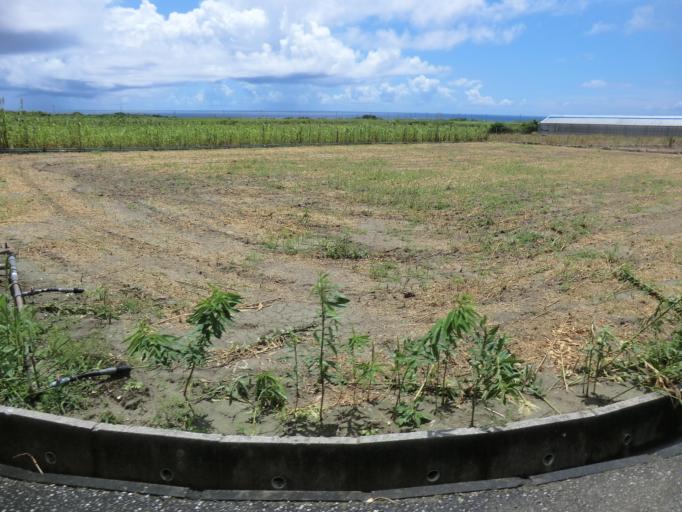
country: JP
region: Okinawa
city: Itoman
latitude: 26.0849
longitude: 127.6717
